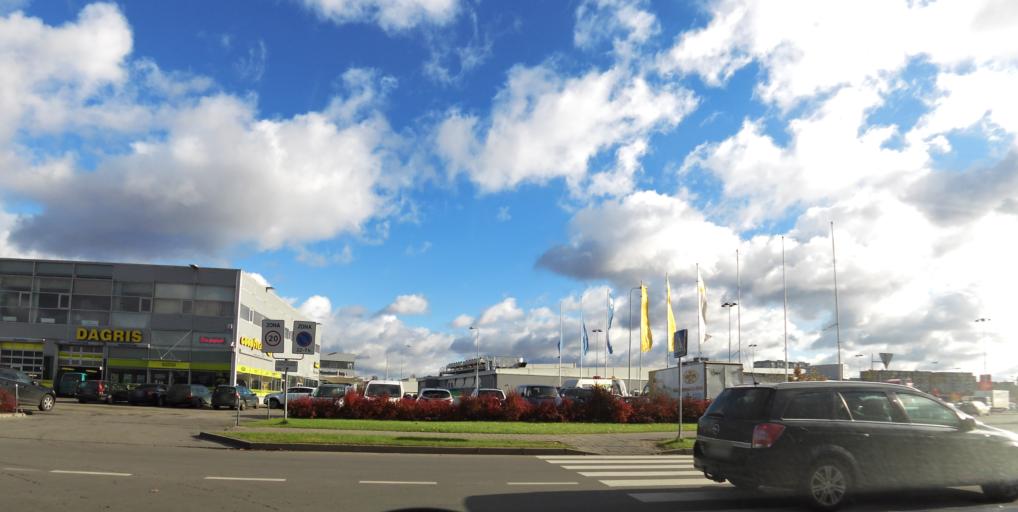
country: LT
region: Vilnius County
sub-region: Vilnius
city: Vilnius
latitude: 54.7133
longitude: 25.2995
